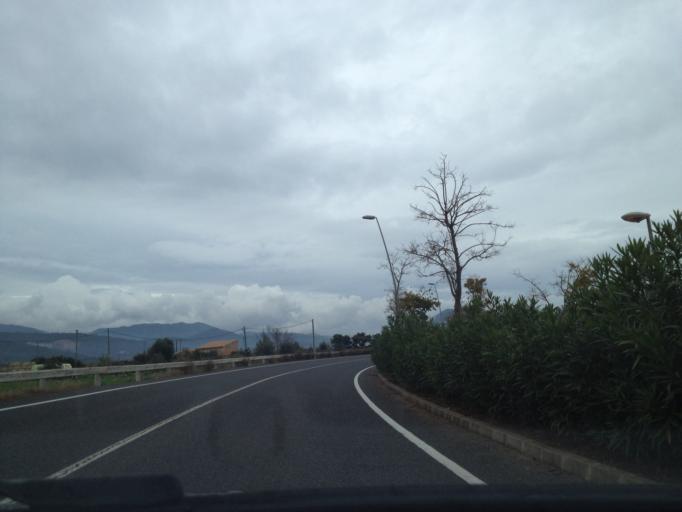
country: ES
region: Balearic Islands
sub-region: Illes Balears
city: sa Pobla
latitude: 39.7702
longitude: 3.0120
